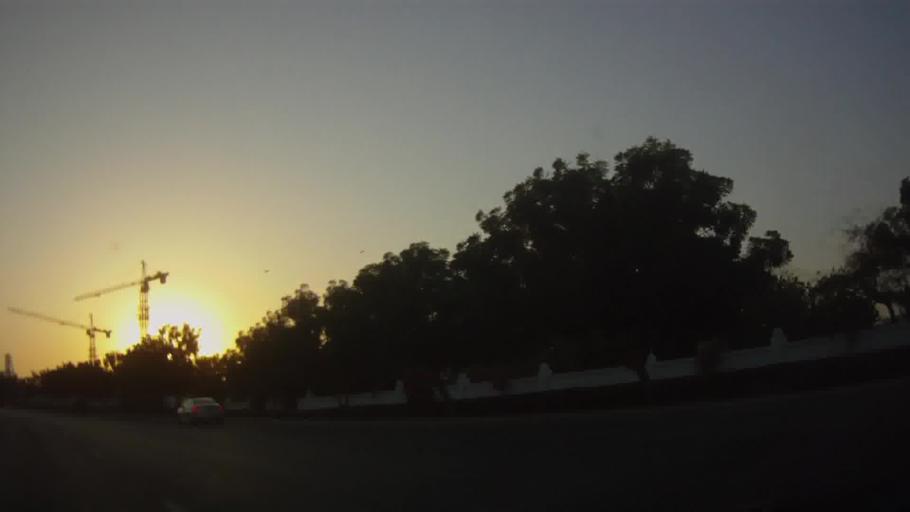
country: OM
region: Muhafazat Masqat
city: Bawshar
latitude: 23.6152
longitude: 58.4687
